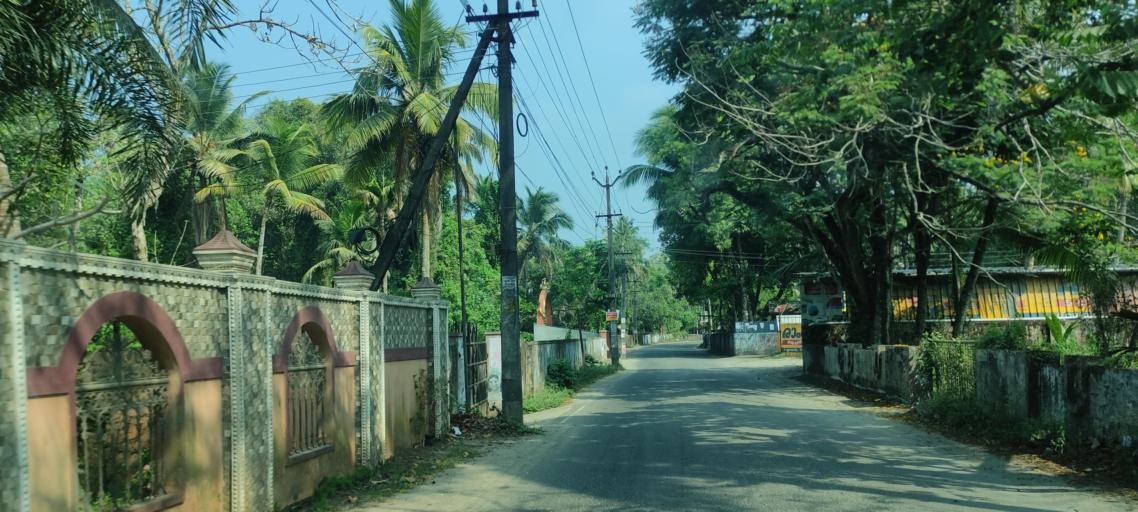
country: IN
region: Kerala
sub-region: Alappuzha
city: Kutiatodu
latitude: 9.7899
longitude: 76.3032
